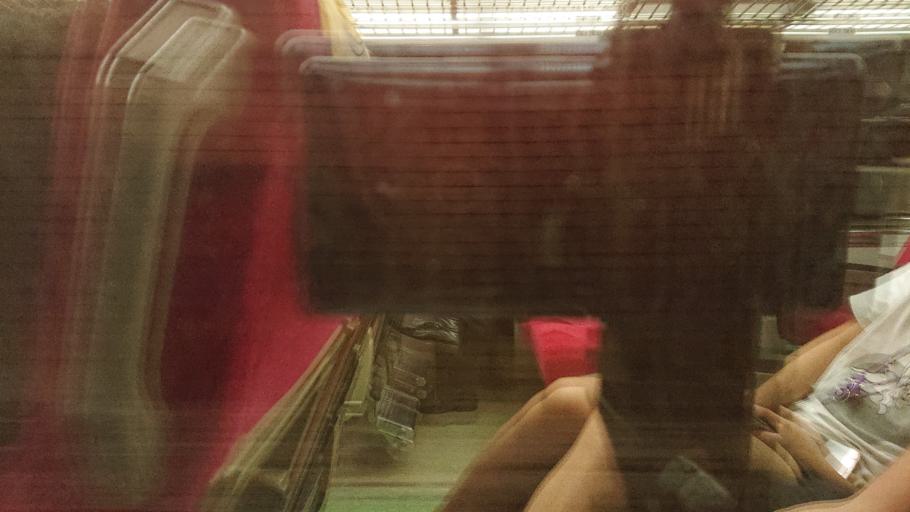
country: TW
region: Taiwan
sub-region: Keelung
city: Keelung
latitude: 25.1084
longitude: 121.8137
